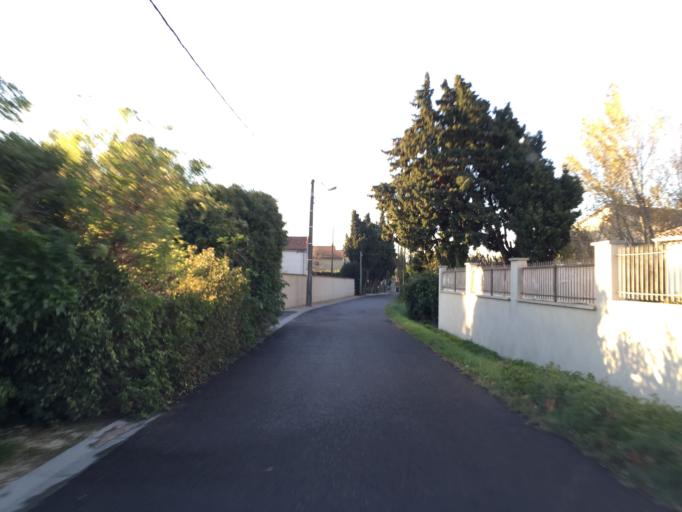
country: FR
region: Provence-Alpes-Cote d'Azur
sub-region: Departement du Vaucluse
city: Courthezon
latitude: 44.0854
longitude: 4.8803
